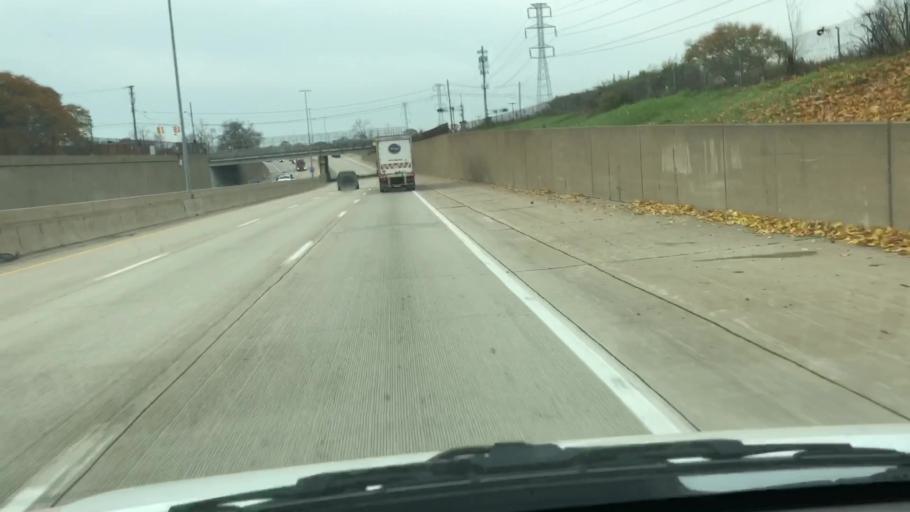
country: US
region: Michigan
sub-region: Wayne County
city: Lincoln Park
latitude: 42.2484
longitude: -83.1902
